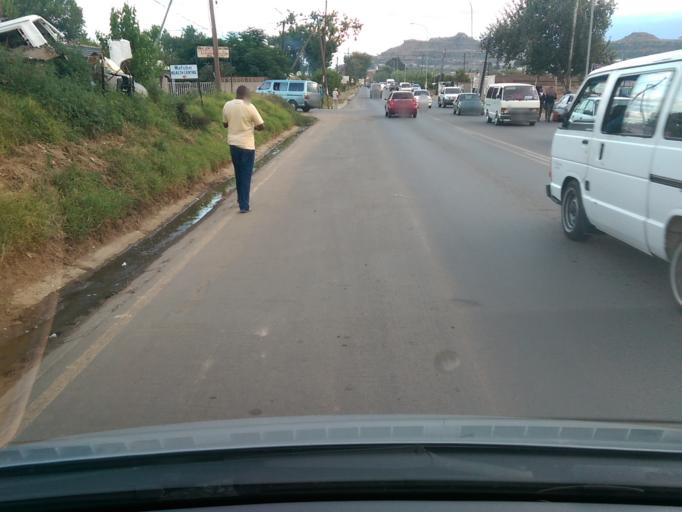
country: LS
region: Maseru
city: Maseru
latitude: -29.3063
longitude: 27.5174
